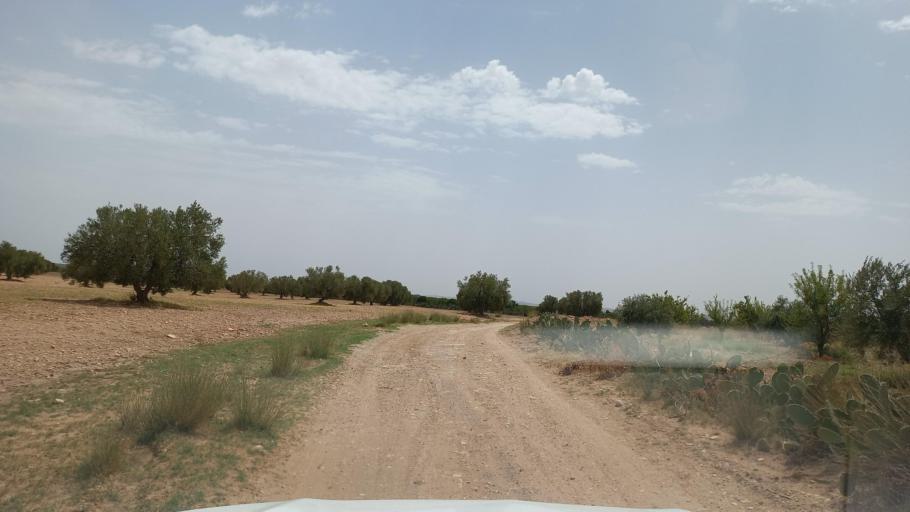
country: TN
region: Al Qasrayn
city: Kasserine
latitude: 35.2919
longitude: 9.0202
